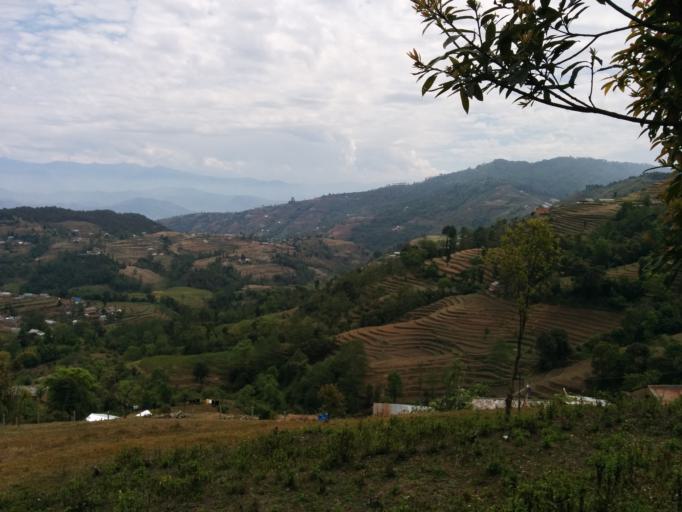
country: NP
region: Central Region
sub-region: Bagmati Zone
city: Nagarkot
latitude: 27.7422
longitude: 85.4976
